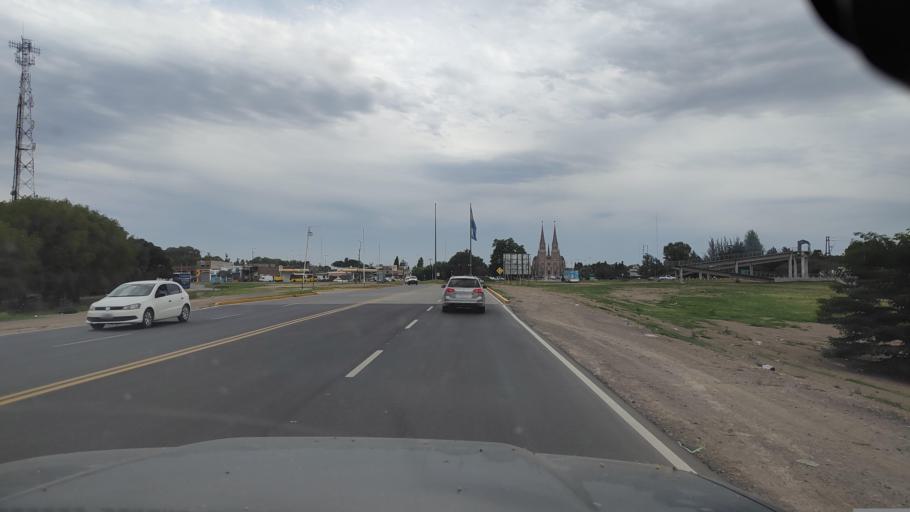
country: AR
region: Buenos Aires
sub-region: Partido de Lujan
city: Lujan
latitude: -34.5539
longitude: -59.1170
